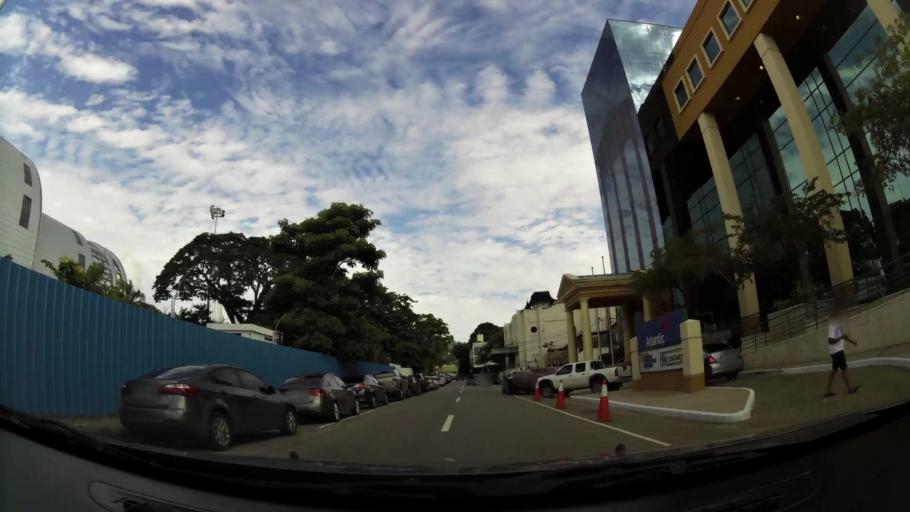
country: TT
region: City of Port of Spain
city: Port-of-Spain
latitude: 10.6626
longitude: -61.5112
